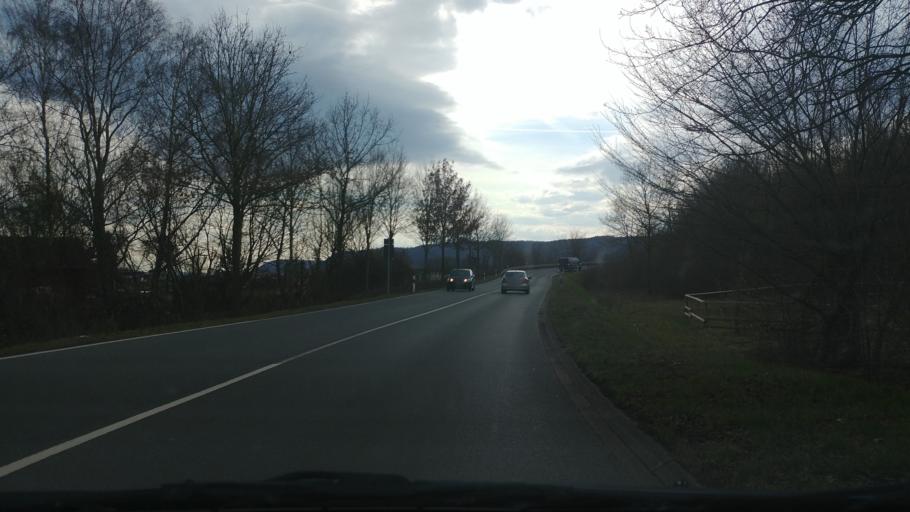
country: DE
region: Lower Saxony
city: Holzminden
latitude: 51.8311
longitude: 9.4350
